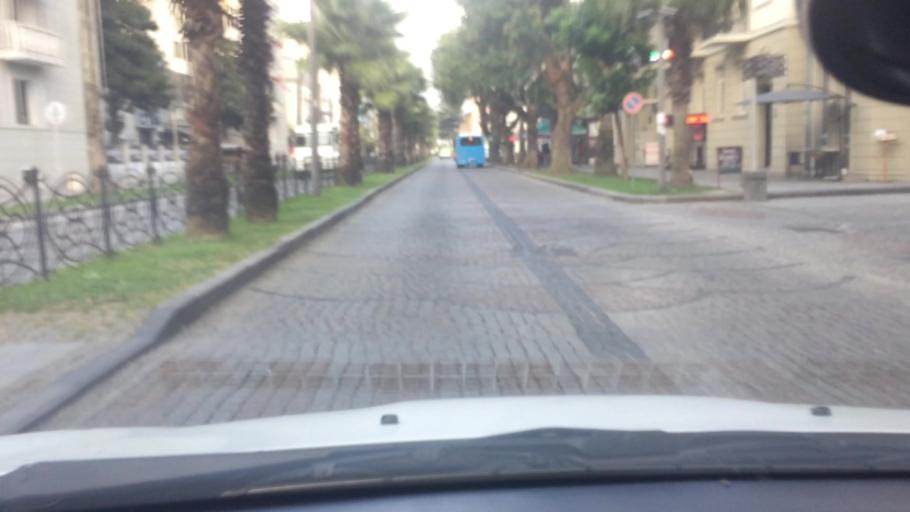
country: GE
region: Ajaria
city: Batumi
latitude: 41.6519
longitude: 41.6347
